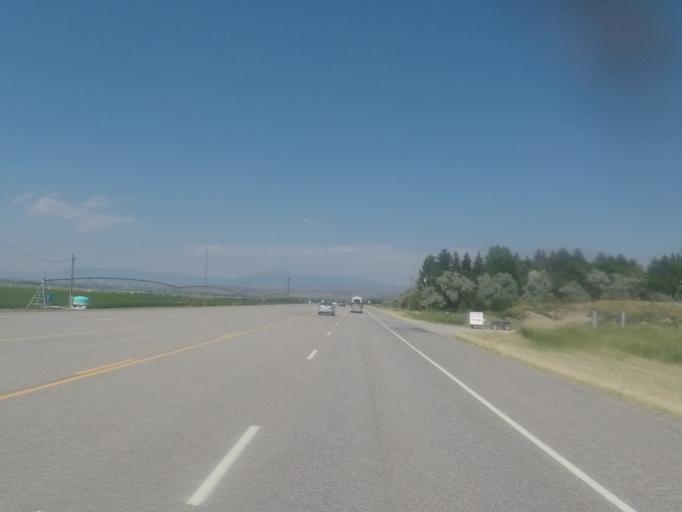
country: US
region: Montana
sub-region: Broadwater County
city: Townsend
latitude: 46.1404
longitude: -111.4776
